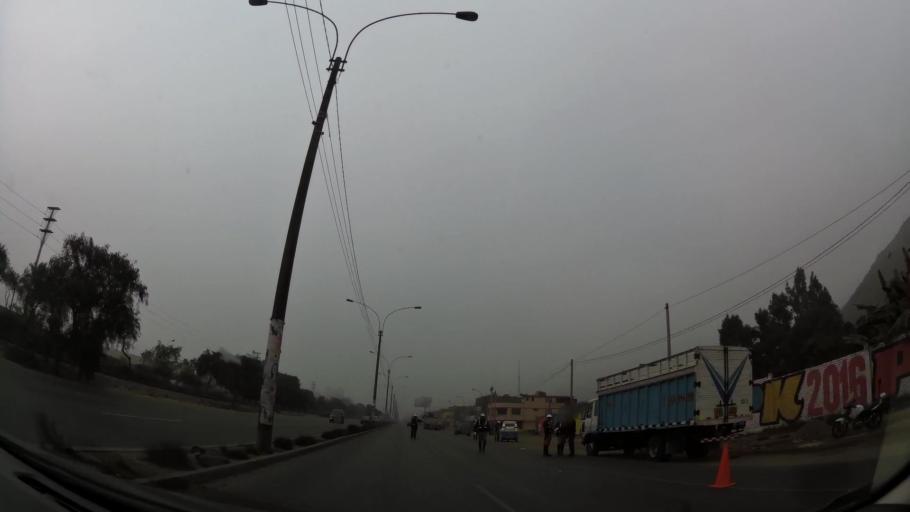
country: PE
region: Lima
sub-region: Lima
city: Santa Maria
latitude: -11.9945
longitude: -76.8306
